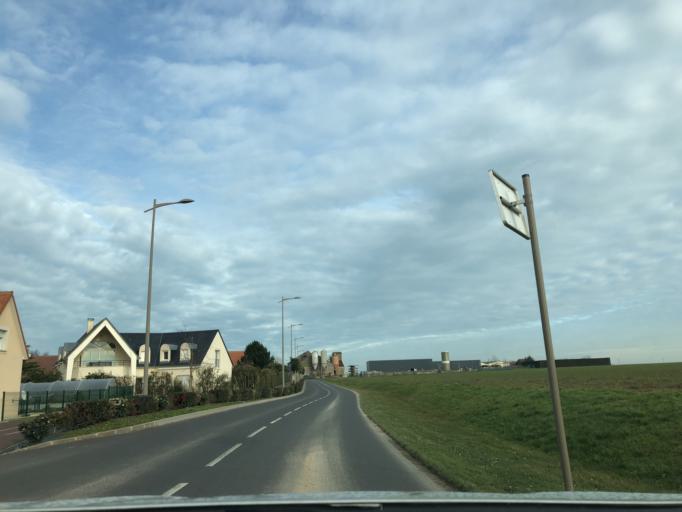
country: FR
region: Lower Normandy
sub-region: Departement du Calvados
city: Douvres-la-Delivrande
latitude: 49.2919
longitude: -0.3691
